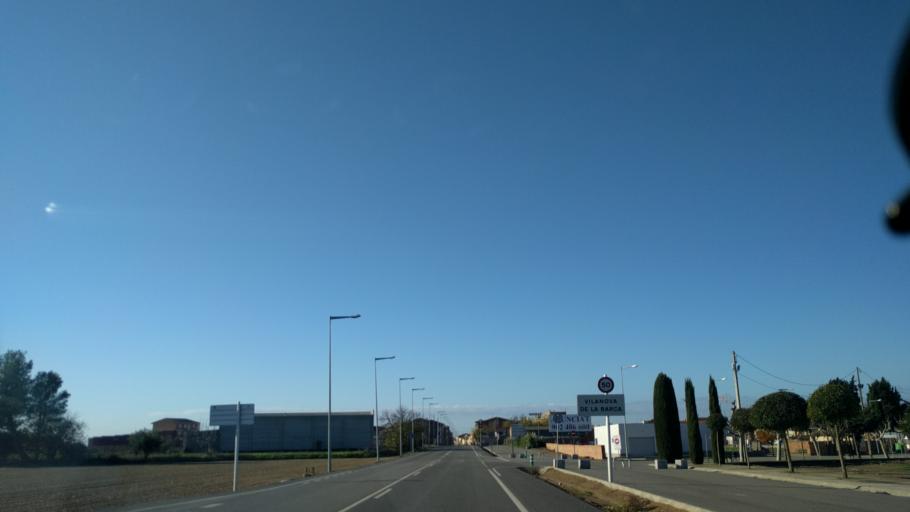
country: ES
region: Catalonia
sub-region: Provincia de Lleida
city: Corbins
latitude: 41.6910
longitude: 0.7319
